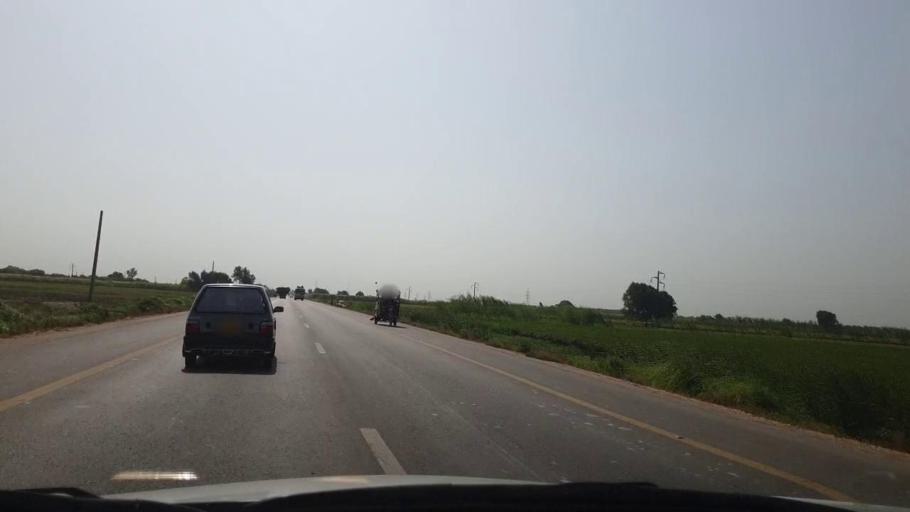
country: PK
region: Sindh
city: Tando Muhammad Khan
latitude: 25.1127
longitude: 68.5784
